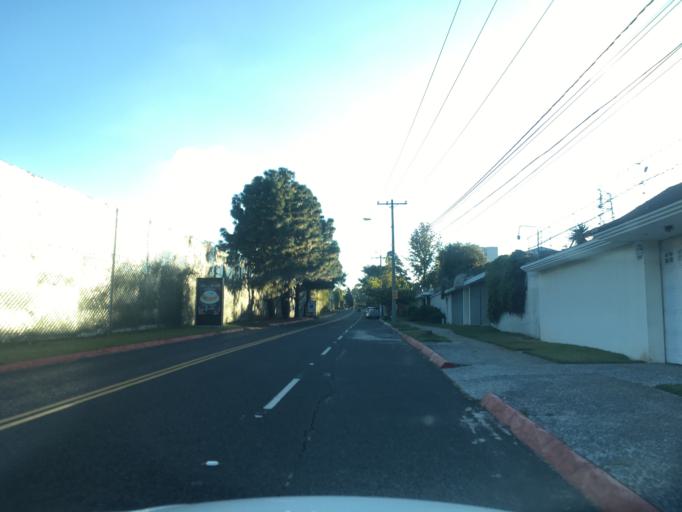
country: GT
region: Guatemala
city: Santa Catarina Pinula
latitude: 14.6057
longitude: -90.4862
